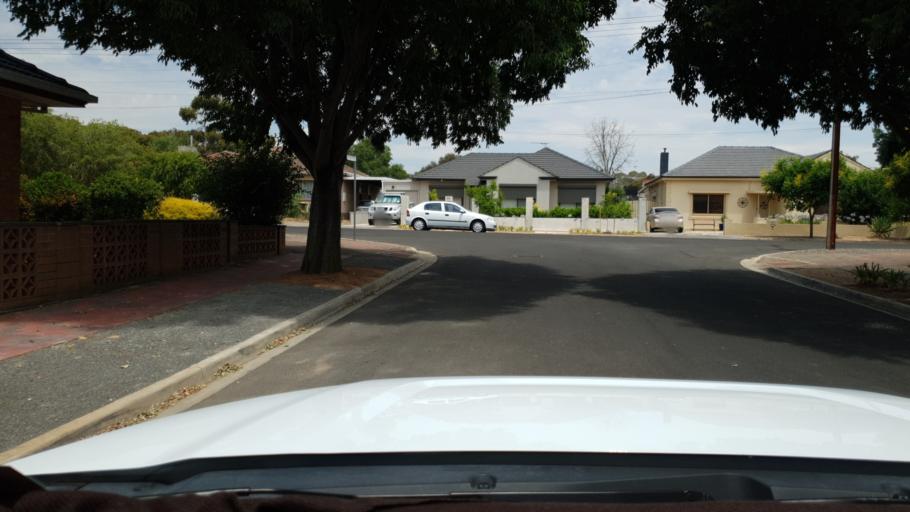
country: AU
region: South Australia
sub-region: Marion
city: Clovelly Park
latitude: -35.0027
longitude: 138.5804
